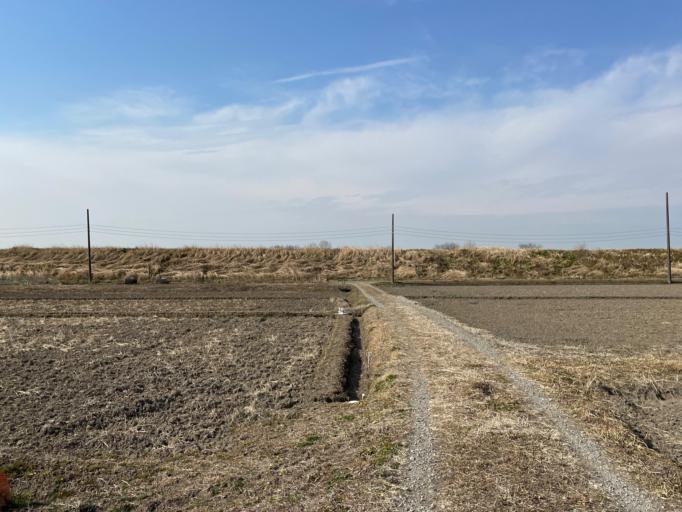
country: JP
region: Saitama
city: Shiki
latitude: 35.8432
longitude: 139.5984
